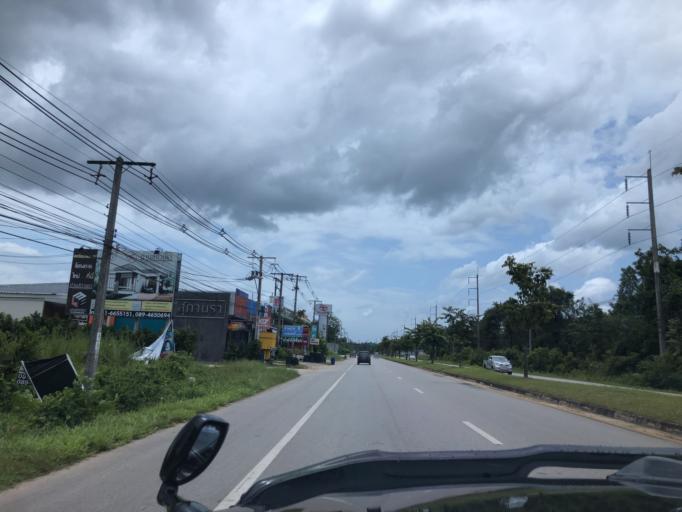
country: TH
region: Krabi
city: Khlong Thom
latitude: 7.9732
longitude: 99.1398
